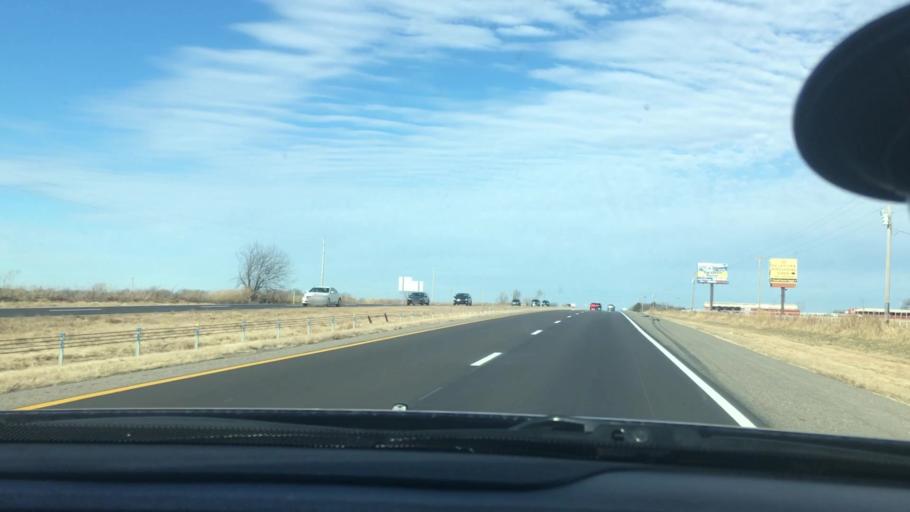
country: US
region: Oklahoma
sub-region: Cleveland County
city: Noble
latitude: 35.0918
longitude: -97.4199
